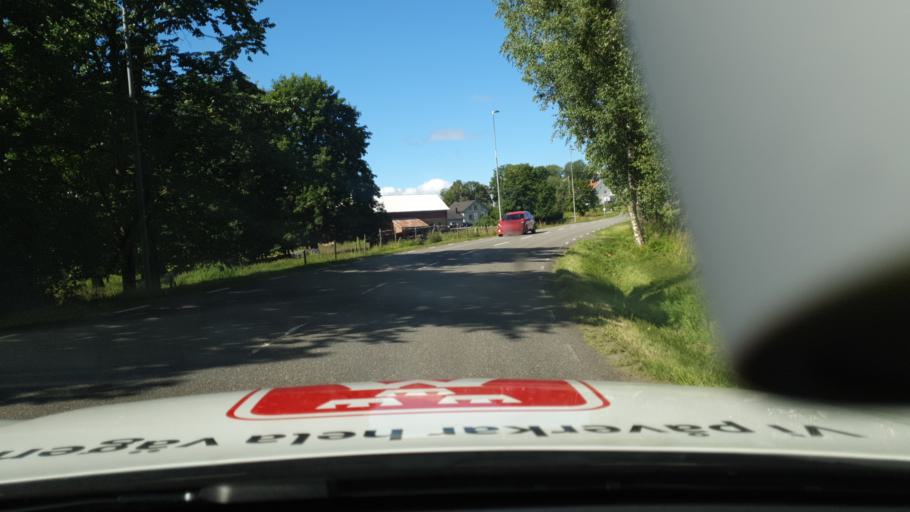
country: SE
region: Vaestra Goetaland
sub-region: Falkopings Kommun
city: Akarp
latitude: 58.2105
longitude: 13.5988
